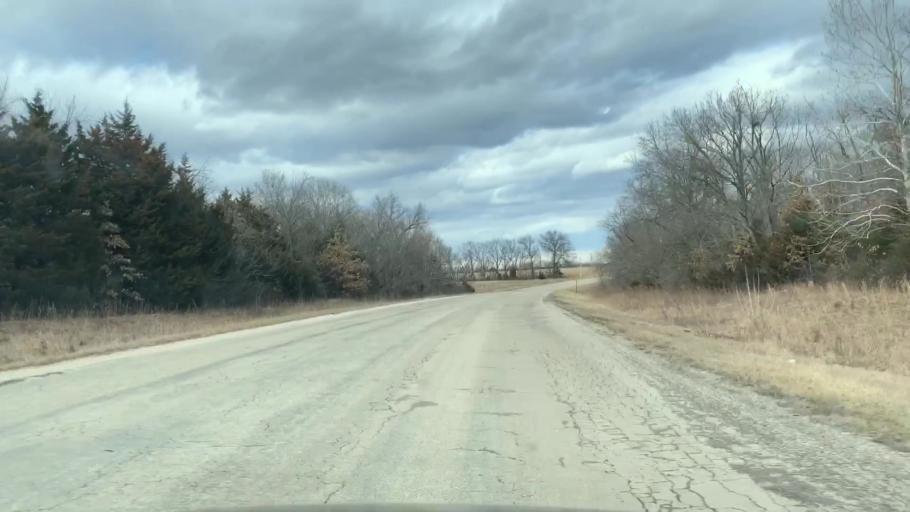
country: US
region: Kansas
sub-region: Allen County
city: Humboldt
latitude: 37.7561
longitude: -95.4719
